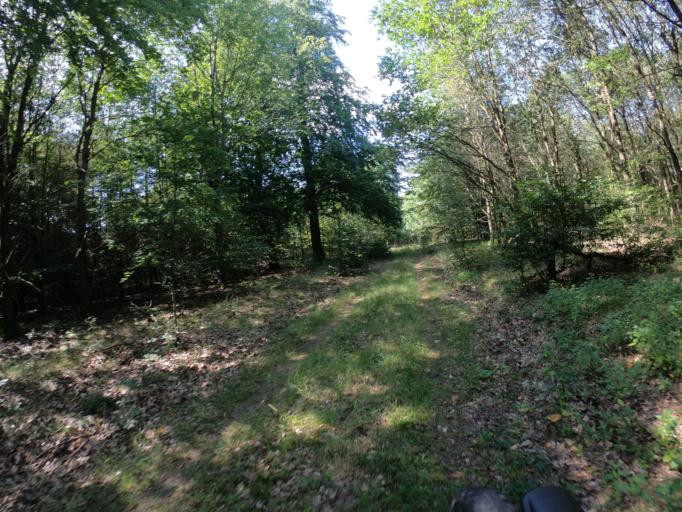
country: DE
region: Hesse
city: Morfelden-Walldorf
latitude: 49.9982
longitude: 8.6238
